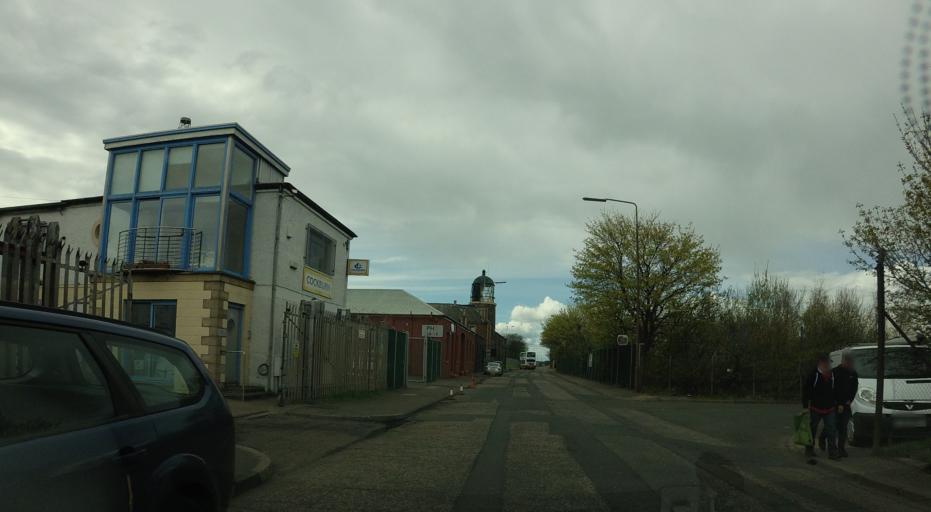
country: GB
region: Scotland
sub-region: Edinburgh
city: Edinburgh
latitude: 55.9818
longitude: -3.2277
